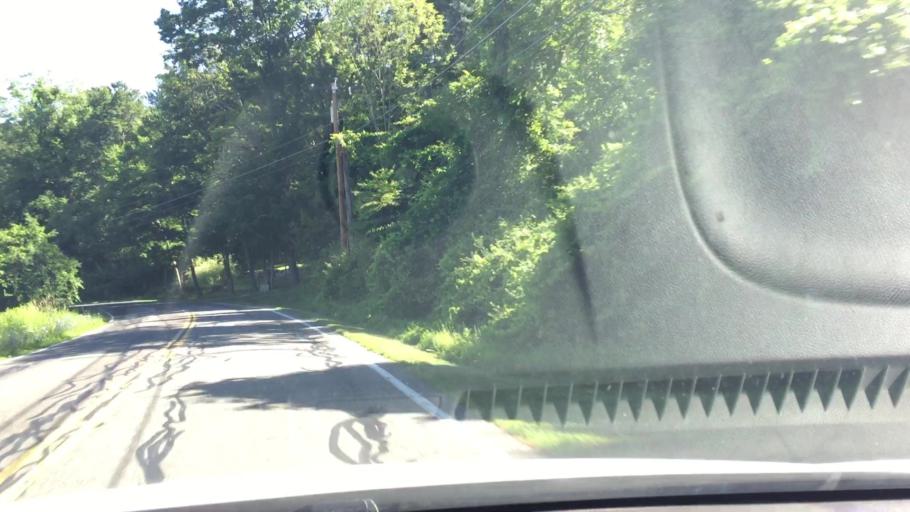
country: US
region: Massachusetts
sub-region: Berkshire County
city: West Stockbridge
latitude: 42.3443
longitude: -73.3650
